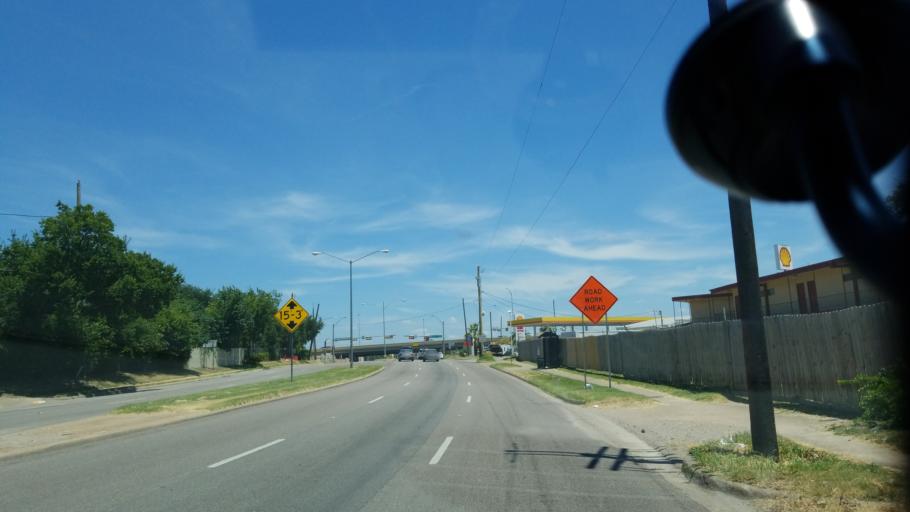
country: US
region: Texas
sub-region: Dallas County
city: Cockrell Hill
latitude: 32.7051
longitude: -96.8345
